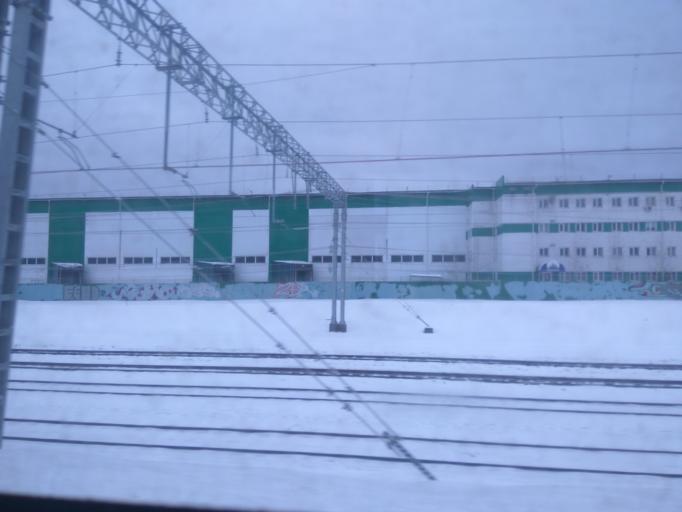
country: RU
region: Moskovskaya
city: Shcherbinka
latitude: 55.4818
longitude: 37.5544
